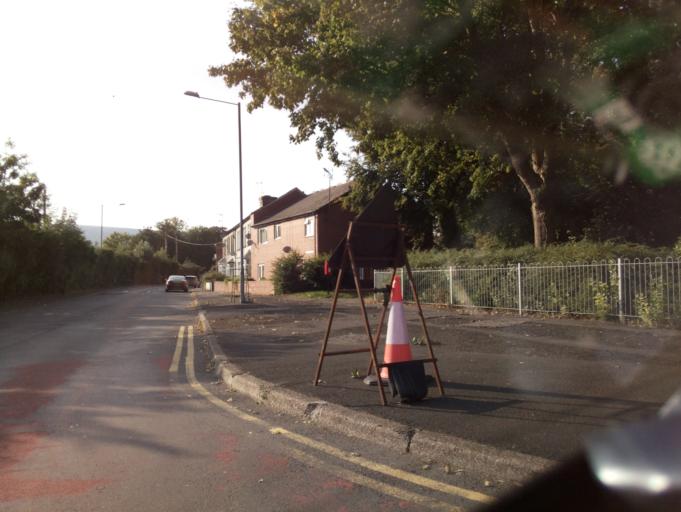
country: GB
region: Wales
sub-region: Torfaen County Borough
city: Cwmbran
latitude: 51.6591
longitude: -3.0130
